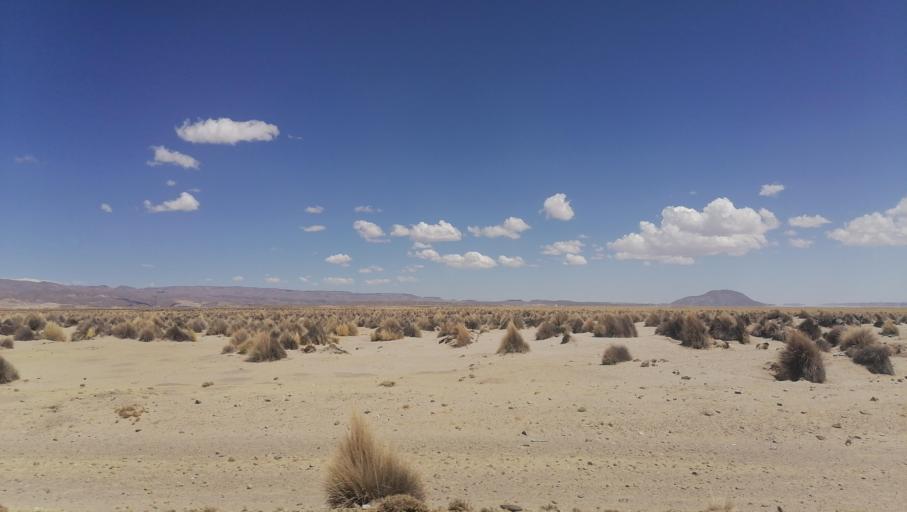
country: BO
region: Oruro
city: Challapata
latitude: -19.1718
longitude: -66.7975
